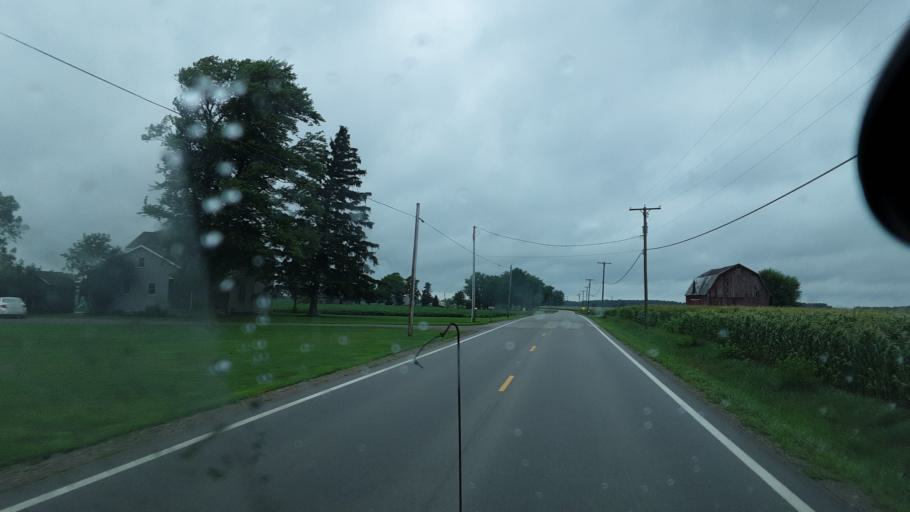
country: US
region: Ohio
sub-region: Van Wert County
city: Van Wert
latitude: 40.7965
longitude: -84.6149
